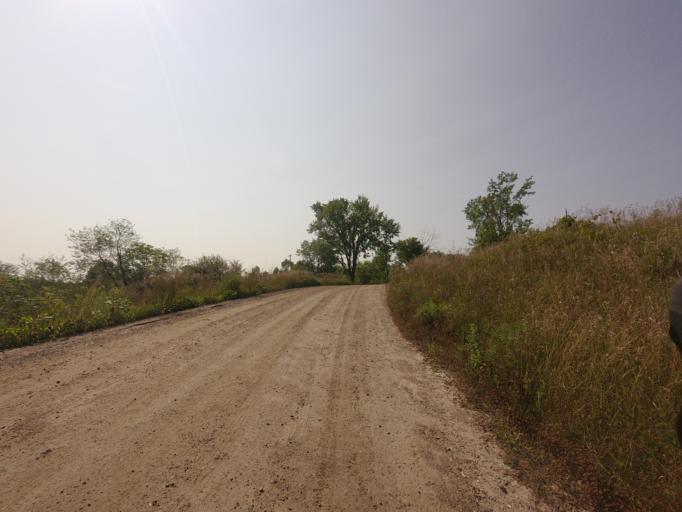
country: CA
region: Ontario
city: Skatepark
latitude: 44.6909
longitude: -76.7491
